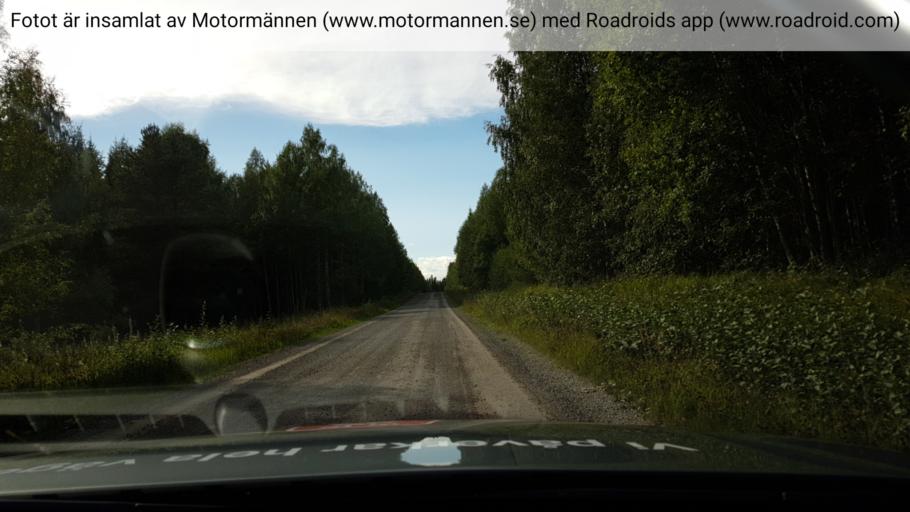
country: SE
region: Jaemtland
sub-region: Braecke Kommun
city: Braecke
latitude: 63.2104
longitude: 15.3873
